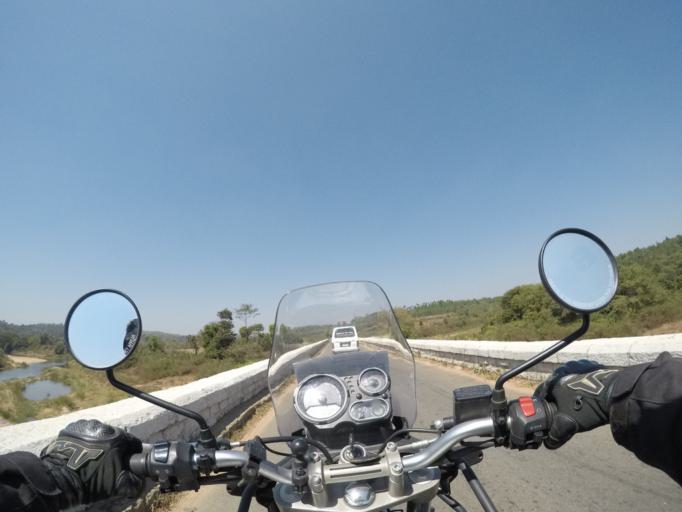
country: IN
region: Karnataka
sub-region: Chikmagalur
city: Mudigere
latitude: 13.0690
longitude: 75.6793
